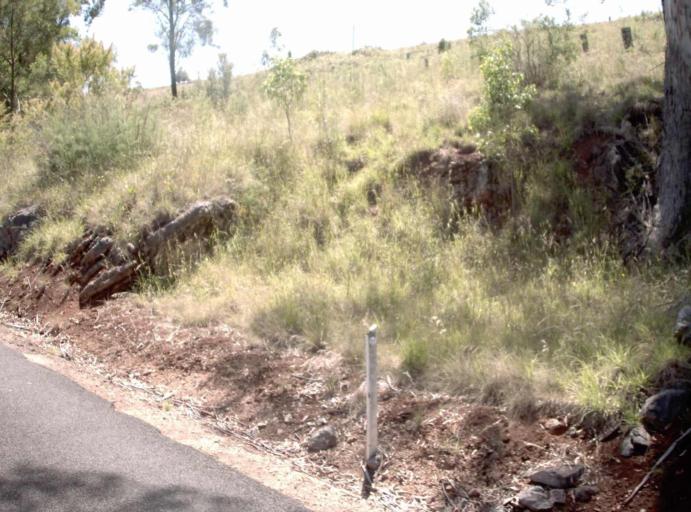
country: AU
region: Victoria
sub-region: East Gippsland
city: Lakes Entrance
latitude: -37.4335
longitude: 148.1975
